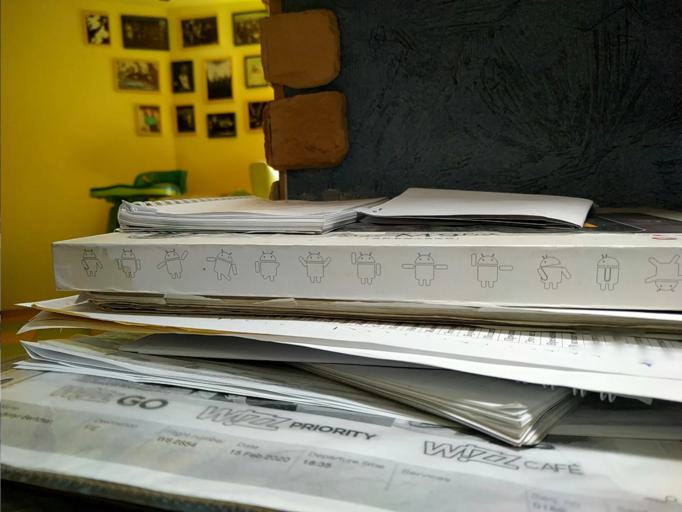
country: RU
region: Novgorod
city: Sol'tsy
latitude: 58.0482
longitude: 30.1829
